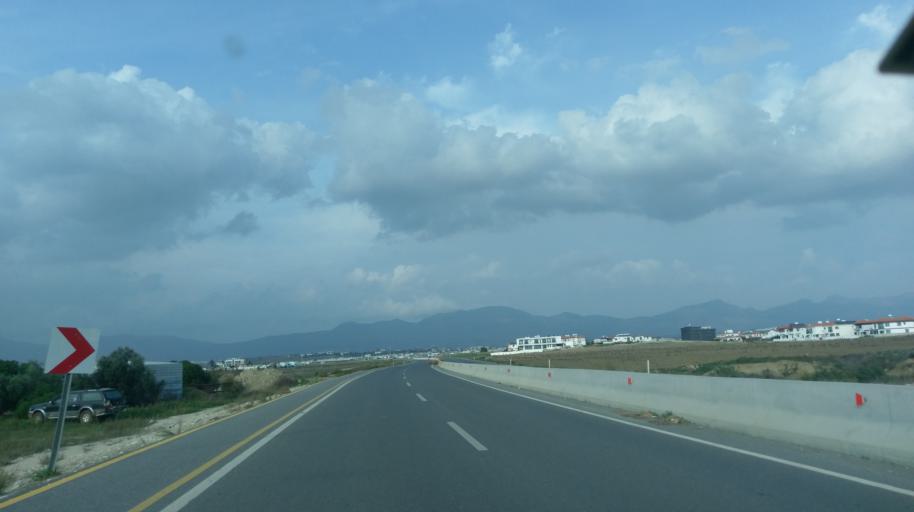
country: CY
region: Lefkosia
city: Nicosia
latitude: 35.2057
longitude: 33.2849
